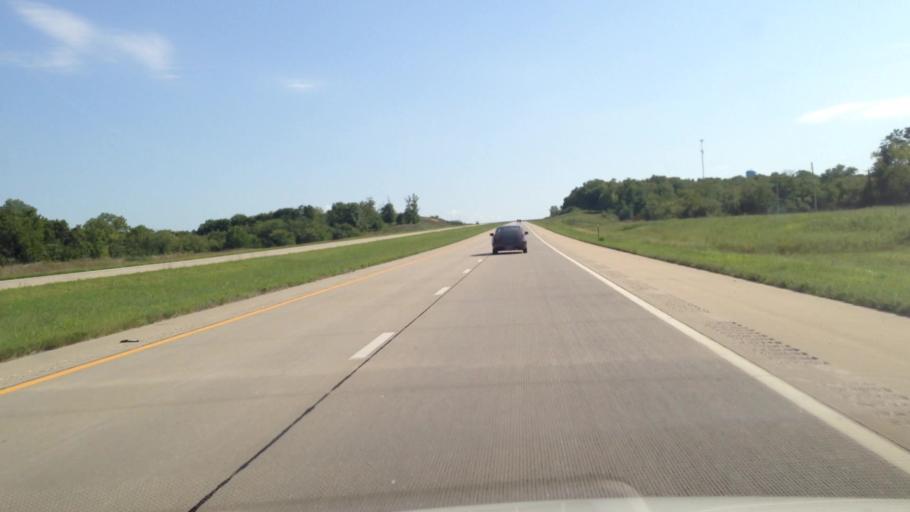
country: US
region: Kansas
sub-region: Linn County
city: Pleasanton
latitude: 38.1215
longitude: -94.7137
